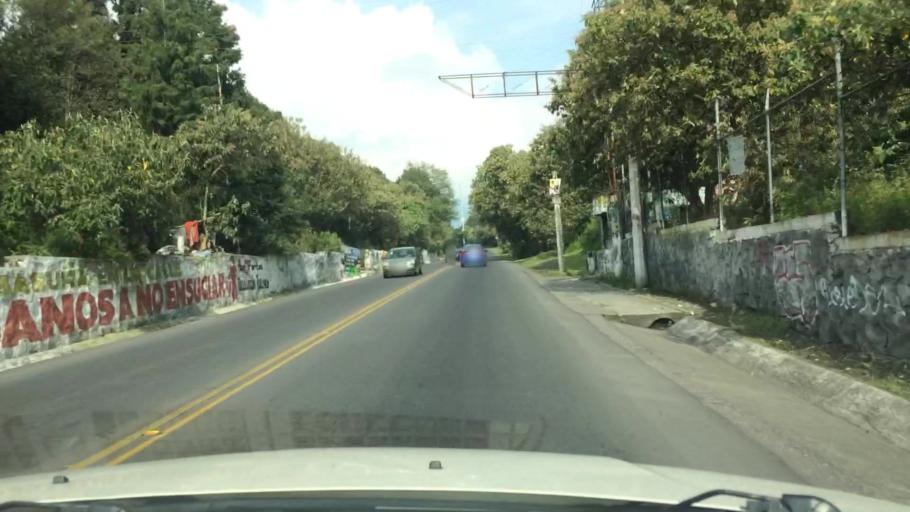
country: MX
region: Mexico City
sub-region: Tlalpan
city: Lomas de Tepemecatl
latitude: 19.2664
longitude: -99.2291
